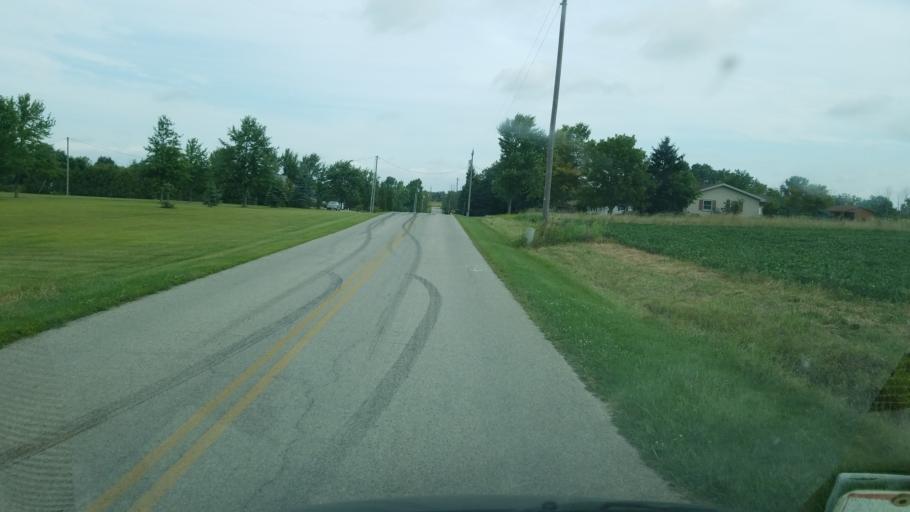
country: US
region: Ohio
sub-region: Seneca County
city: Tiffin
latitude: 41.1207
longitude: -83.0942
